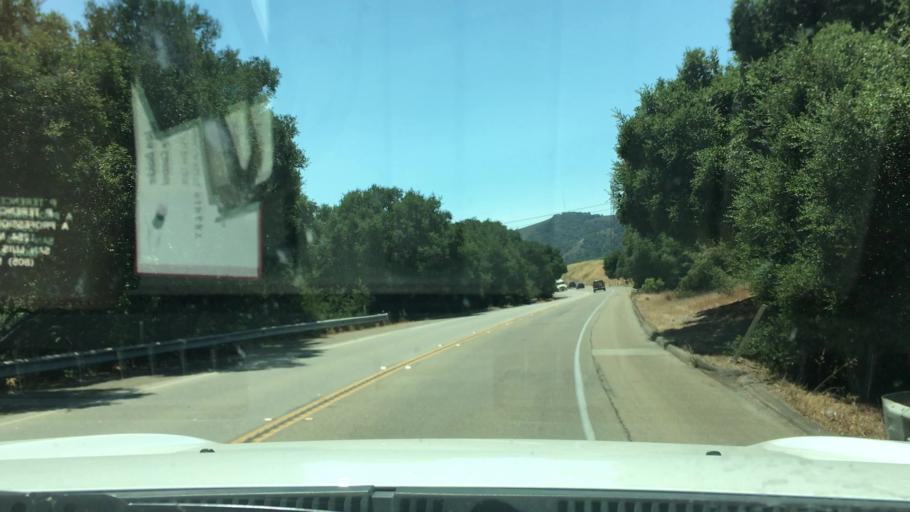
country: US
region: California
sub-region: San Luis Obispo County
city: Pismo Beach
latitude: 35.1743
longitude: -120.6227
